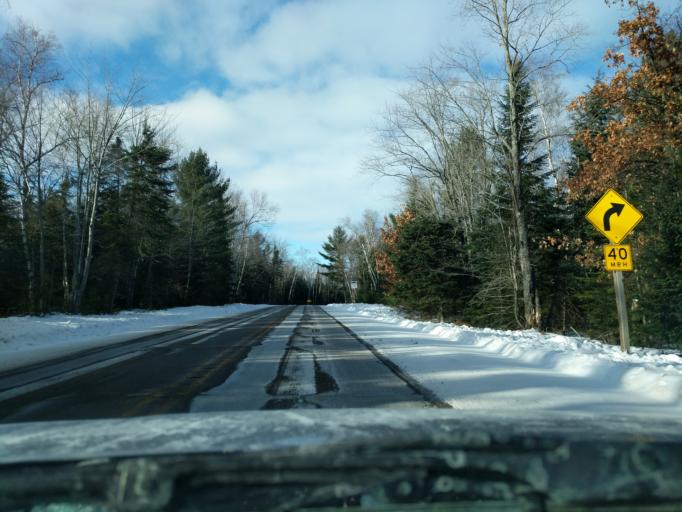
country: US
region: Wisconsin
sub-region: Vilas County
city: Eagle River
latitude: 45.7643
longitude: -89.0668
